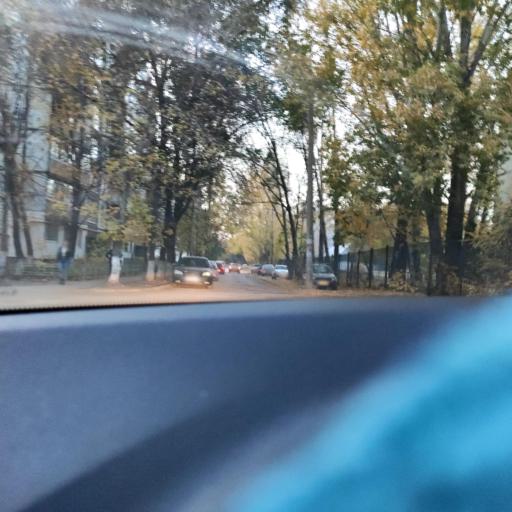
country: RU
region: Samara
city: Samara
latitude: 53.2622
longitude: 50.2297
